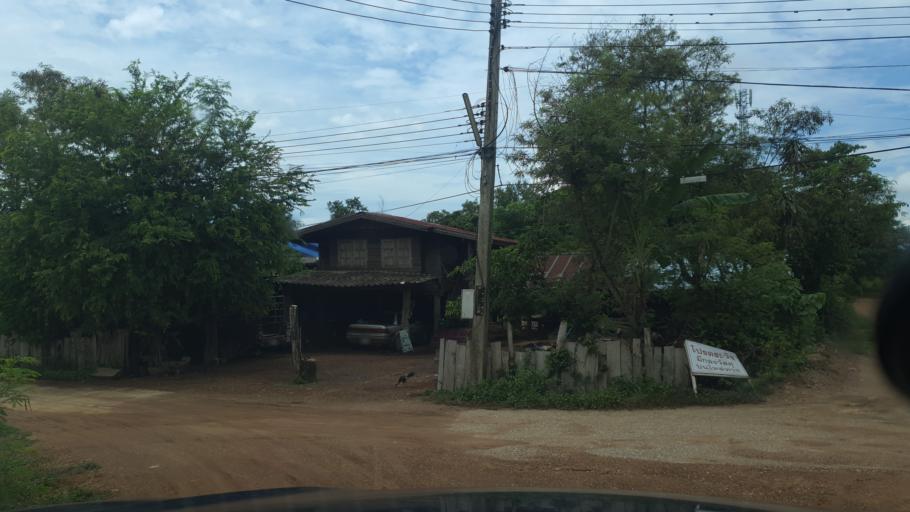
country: TH
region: Lampang
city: Hang Chat
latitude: 18.2881
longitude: 99.3729
